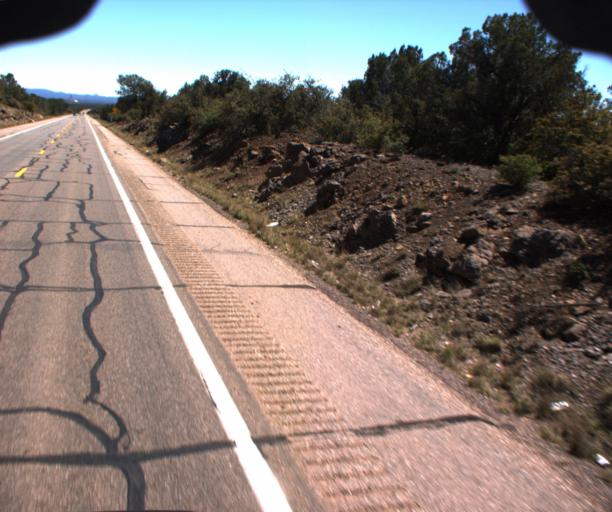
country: US
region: Arizona
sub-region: Yavapai County
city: Paulden
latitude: 35.0654
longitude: -112.4001
